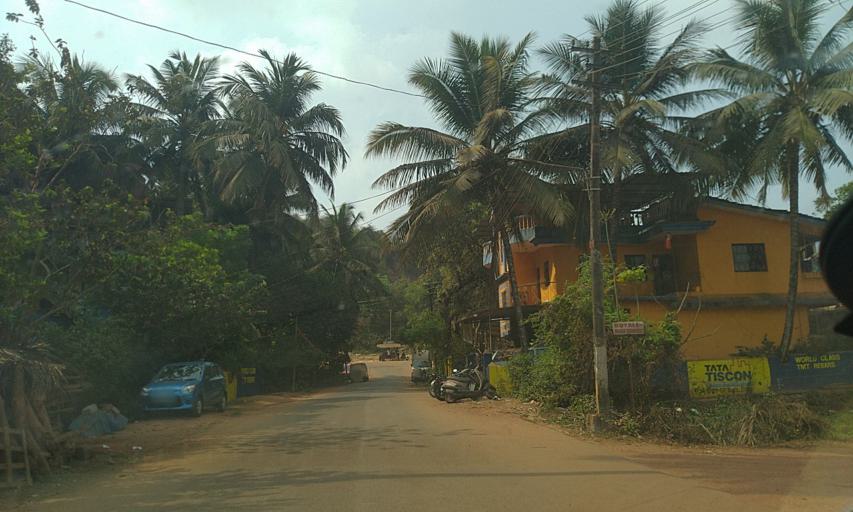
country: IN
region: Goa
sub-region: North Goa
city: Taleigao
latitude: 15.4663
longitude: 73.8275
